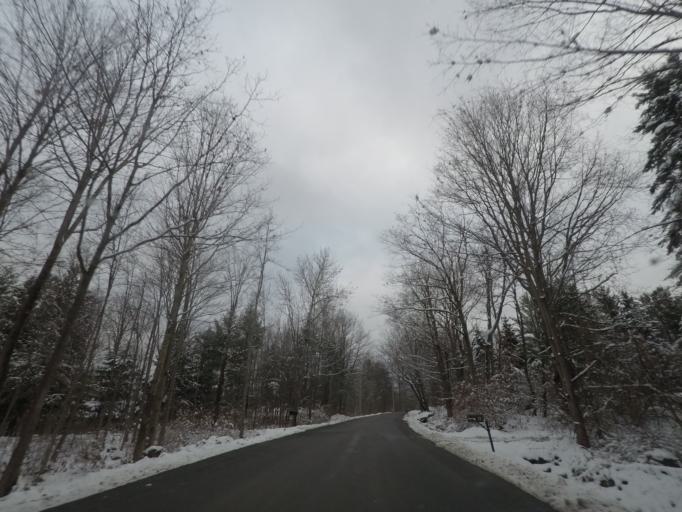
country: US
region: New York
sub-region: Rensselaer County
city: Averill Park
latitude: 42.6571
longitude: -73.5329
